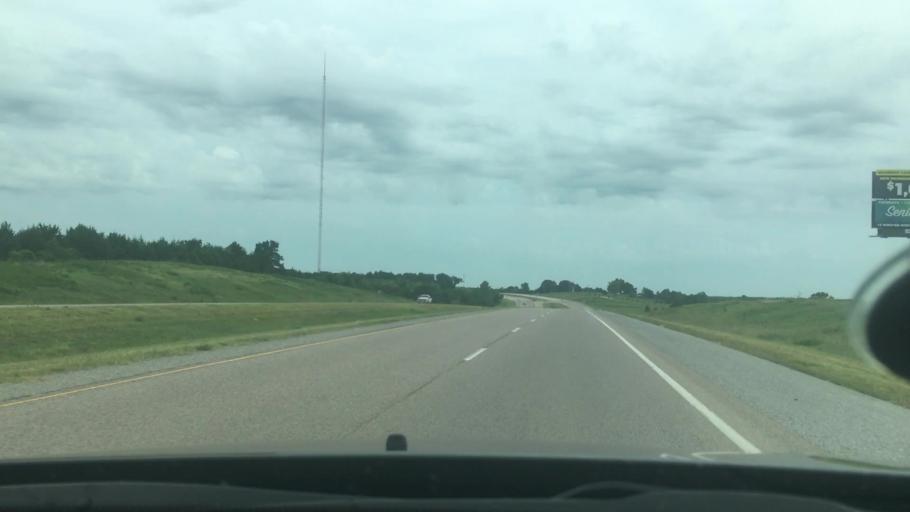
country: US
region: Oklahoma
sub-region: Pontotoc County
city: Byng
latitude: 34.8939
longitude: -96.6749
